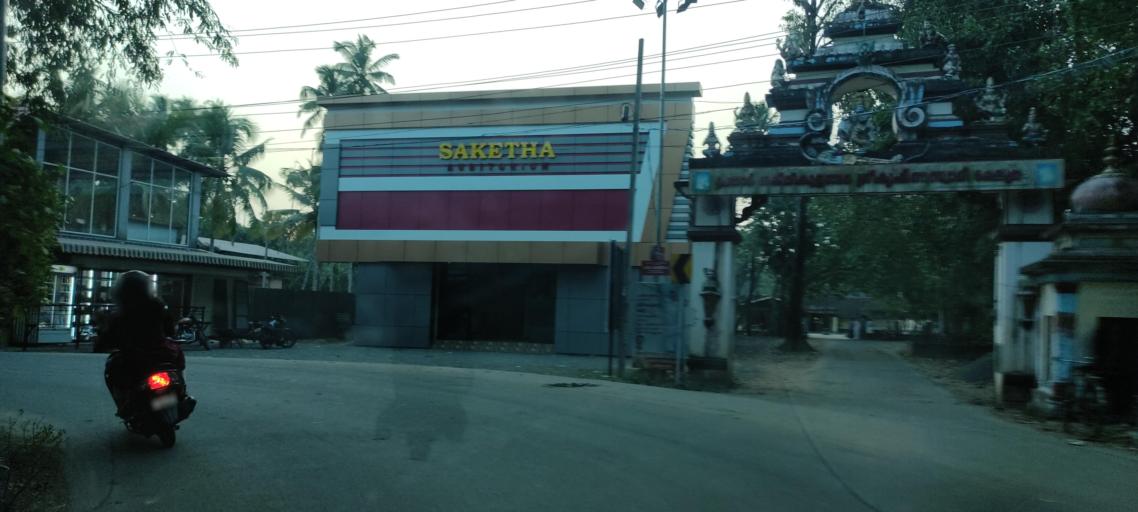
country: IN
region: Kerala
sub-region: Alappuzha
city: Kayankulam
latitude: 9.1252
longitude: 76.4962
